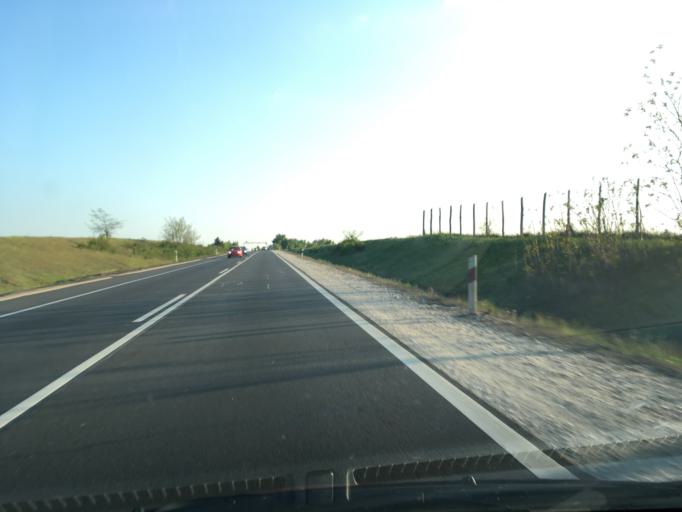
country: HU
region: Pest
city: God
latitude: 47.6636
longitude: 19.1632
